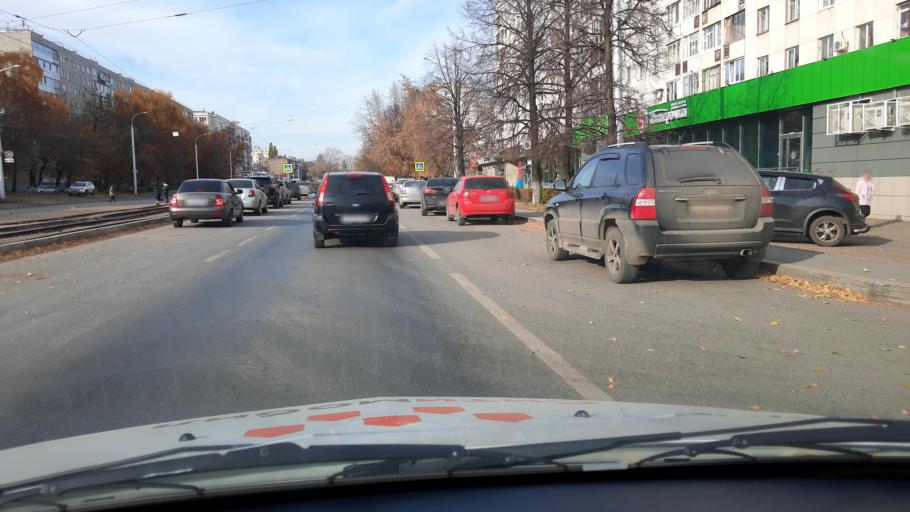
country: RU
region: Bashkortostan
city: Ufa
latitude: 54.8090
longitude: 56.1306
